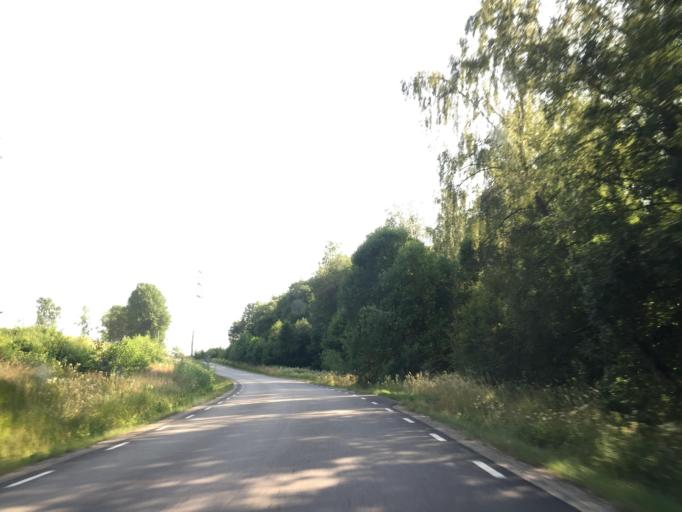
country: SE
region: Vaestra Goetaland
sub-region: Trollhattan
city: Trollhattan
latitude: 58.2820
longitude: 12.2480
